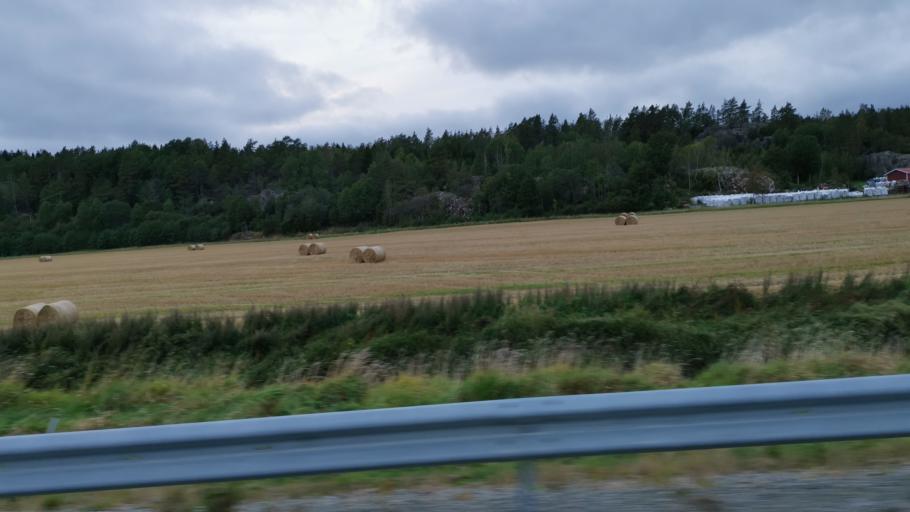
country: SE
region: Vaestra Goetaland
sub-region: Tanums Kommun
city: Tanumshede
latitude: 58.6568
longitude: 11.3455
